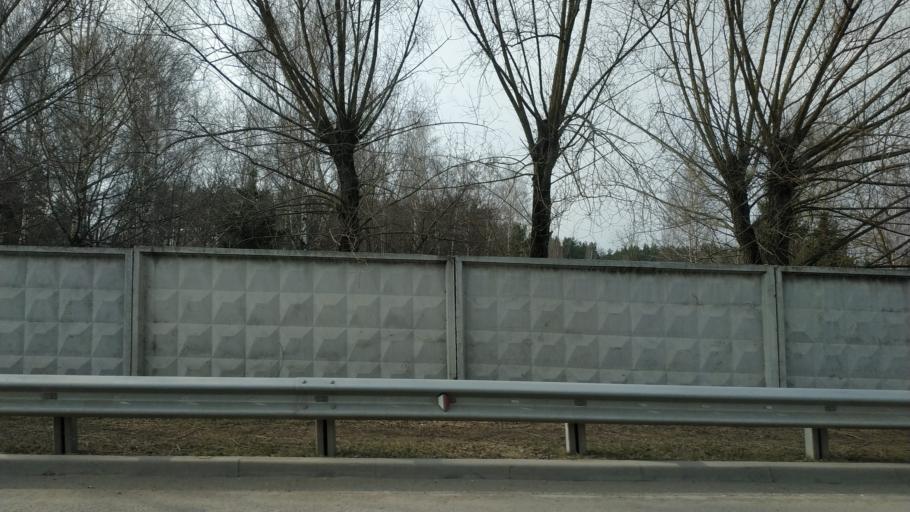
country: RU
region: Moskovskaya
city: Malyshevo
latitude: 55.4931
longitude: 38.3674
